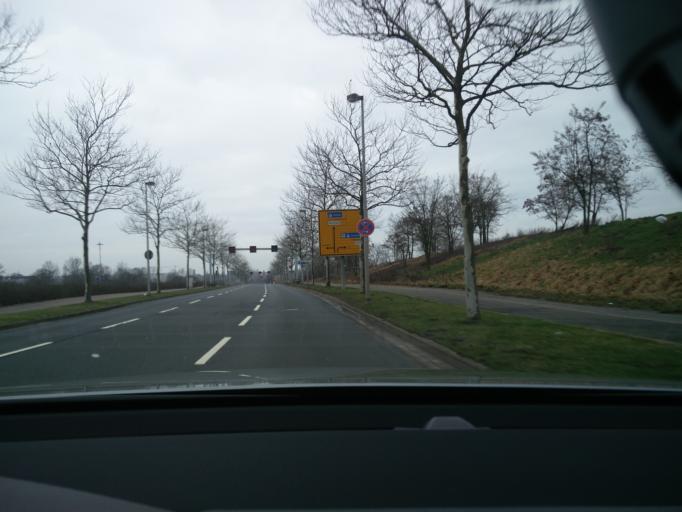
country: DE
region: Lower Saxony
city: Laatzen
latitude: 52.3316
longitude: 9.8183
